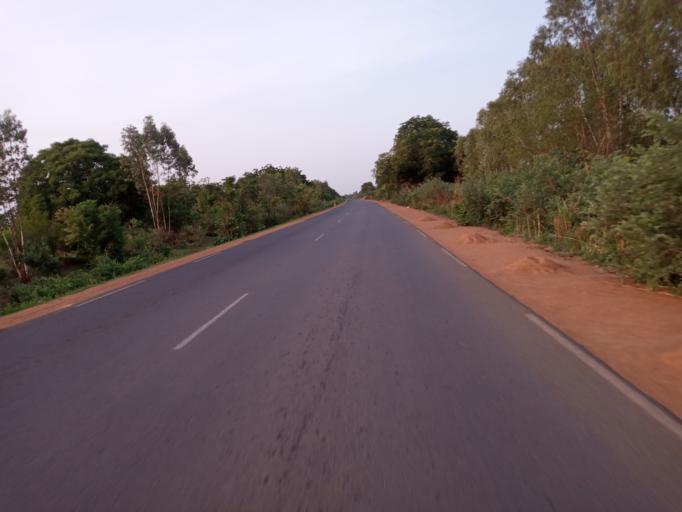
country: ML
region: Bamako
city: Bamako
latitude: 12.2889
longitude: -8.1711
